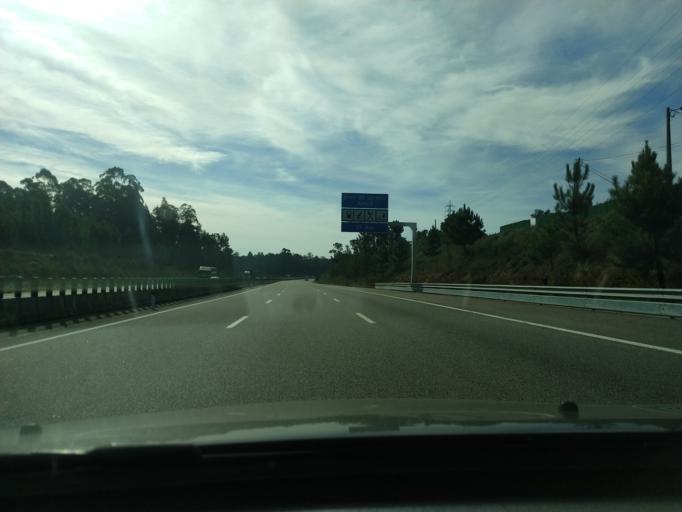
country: PT
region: Aveiro
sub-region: Ovar
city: Valega
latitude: 40.8452
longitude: -8.5570
